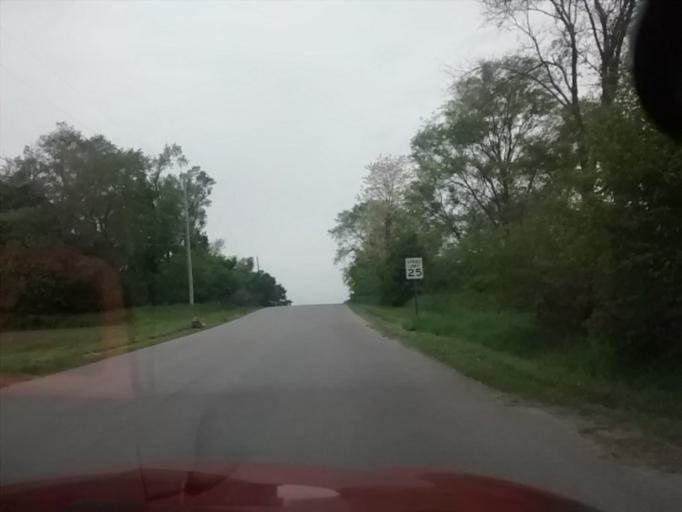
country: US
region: Nebraska
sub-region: Sarpy County
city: Offutt Air Force Base
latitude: 41.1675
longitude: -95.9312
